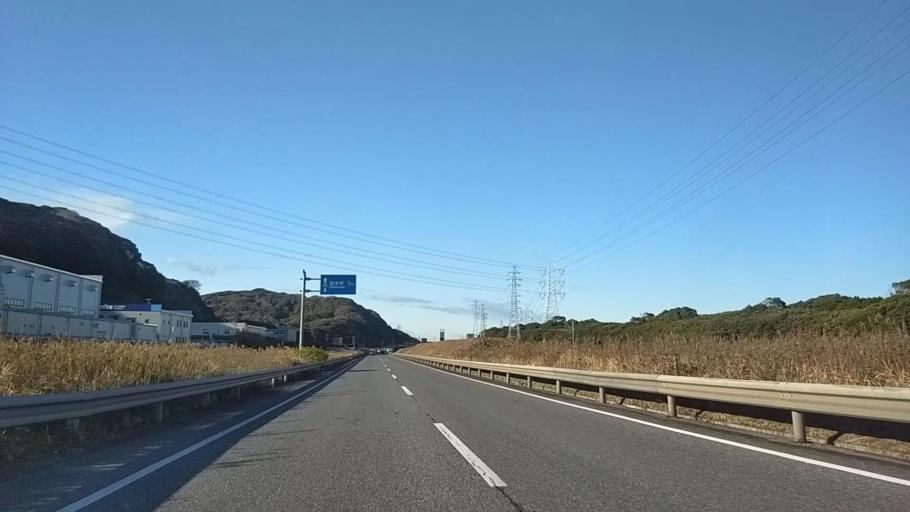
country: JP
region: Chiba
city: Kimitsu
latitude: 35.3477
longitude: 139.8898
